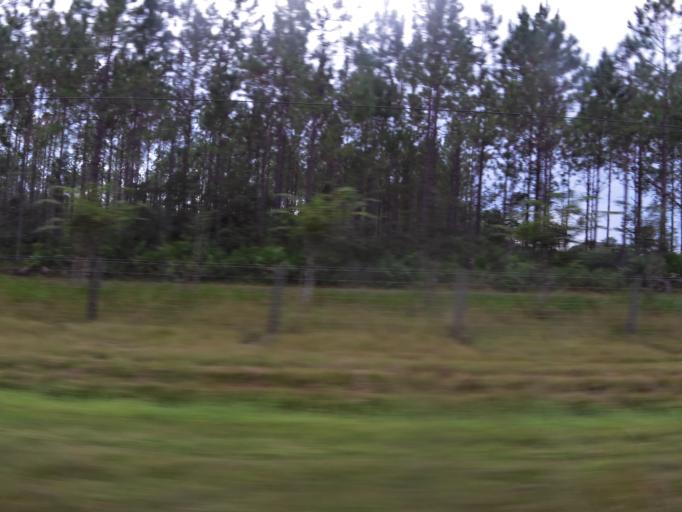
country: US
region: Florida
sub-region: Duval County
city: Baldwin
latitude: 30.3600
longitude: -81.9171
